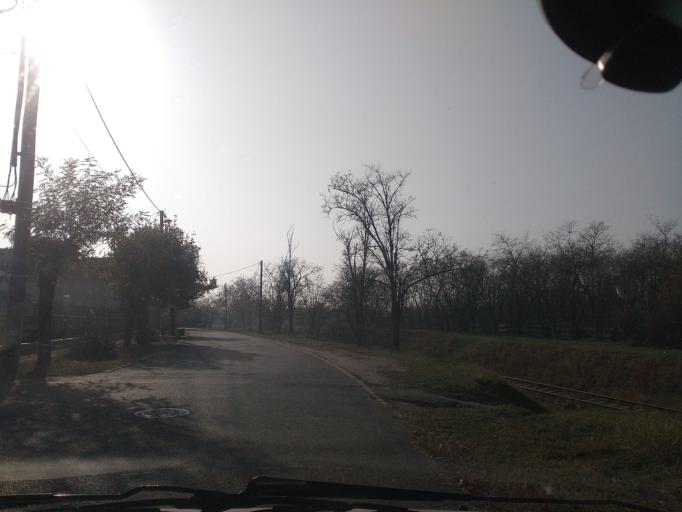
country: HU
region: Budapest
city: Budapest XVIII. keruelet
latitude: 47.4418
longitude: 19.1960
